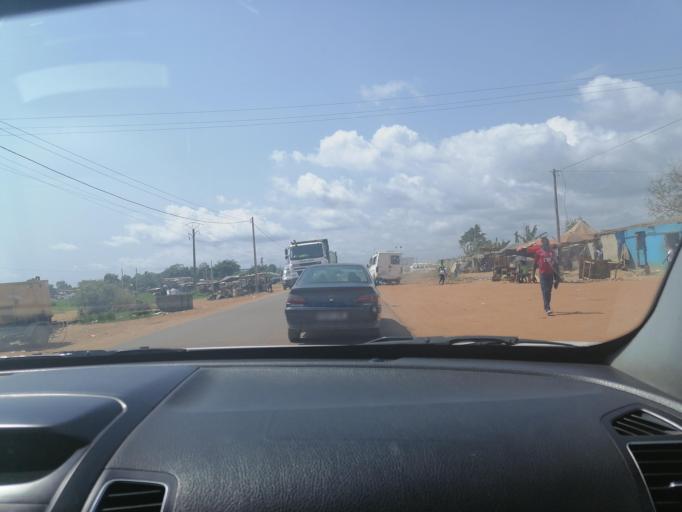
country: CI
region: Lagunes
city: Songon
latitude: 5.3388
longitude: -4.1414
